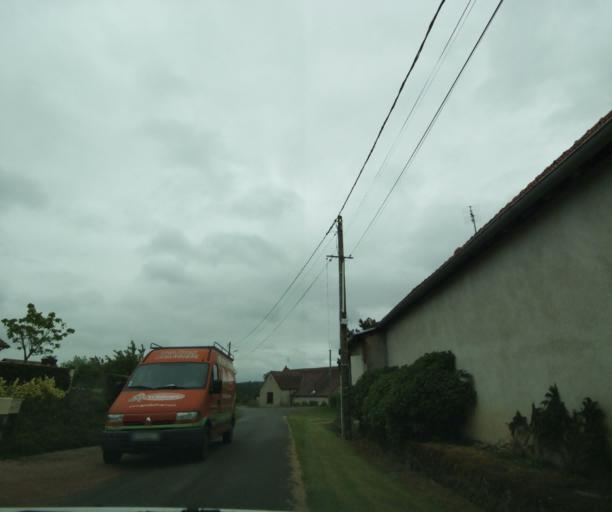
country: FR
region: Bourgogne
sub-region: Departement de Saone-et-Loire
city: Palinges
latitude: 46.4965
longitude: 4.2230
